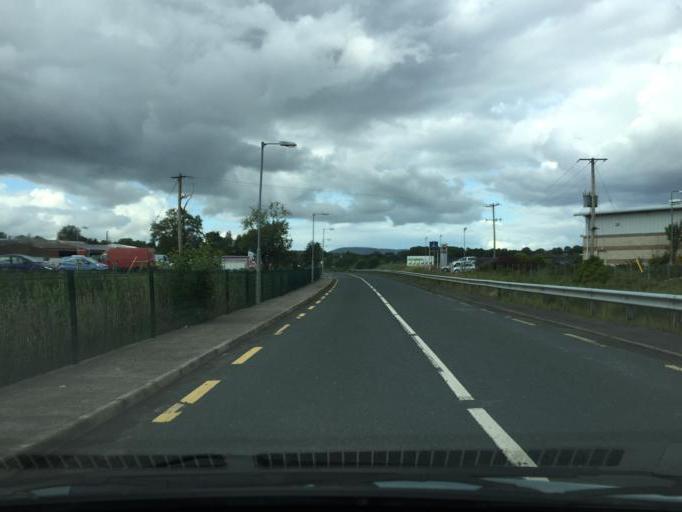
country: IE
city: Ballisodare
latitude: 54.2270
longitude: -8.4933
